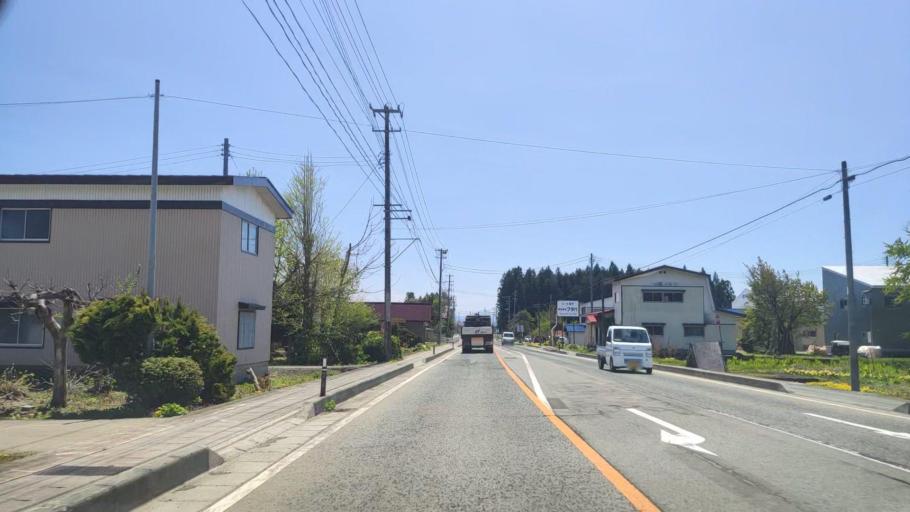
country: JP
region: Yamagata
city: Shinjo
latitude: 38.8252
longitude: 140.3271
